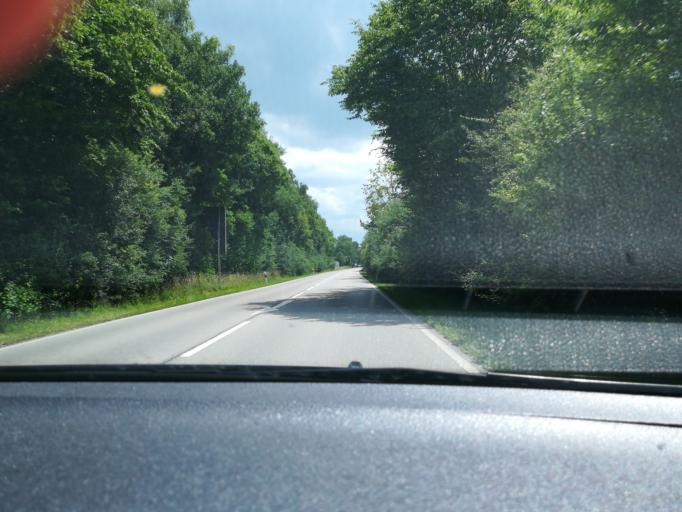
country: DE
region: Bavaria
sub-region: Upper Bavaria
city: Hohenkirchen-Siegertsbrunn
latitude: 48.0249
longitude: 11.6992
